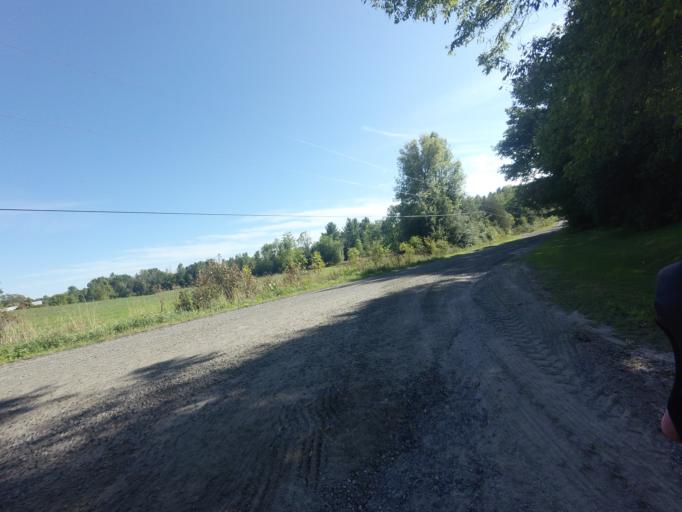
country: CA
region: Ontario
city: Perth
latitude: 44.9361
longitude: -76.3748
